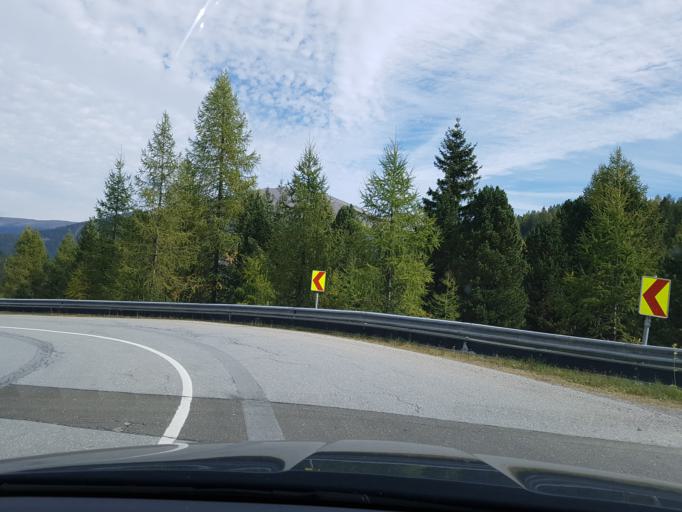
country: AT
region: Carinthia
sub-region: Politischer Bezirk Spittal an der Drau
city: Kleinkirchheim
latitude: 46.9301
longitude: 13.8726
